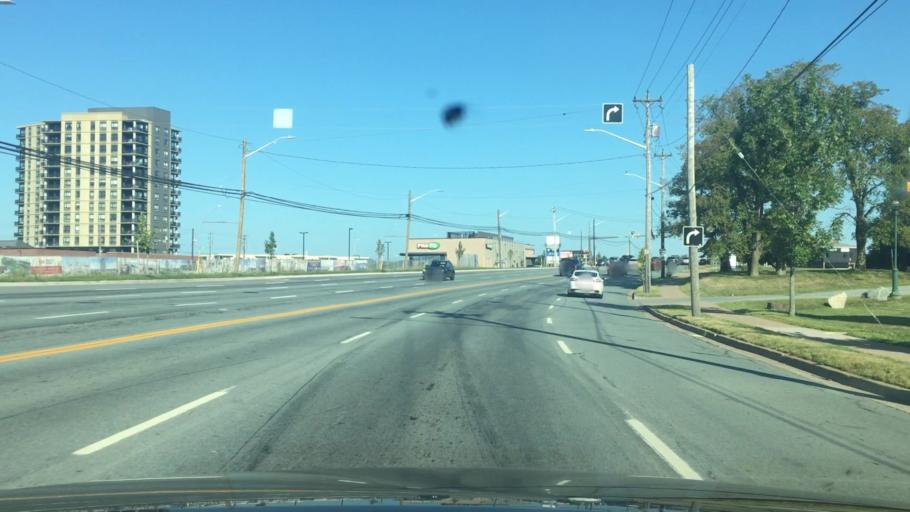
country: CA
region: Nova Scotia
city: Dartmouth
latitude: 44.6990
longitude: -63.6056
